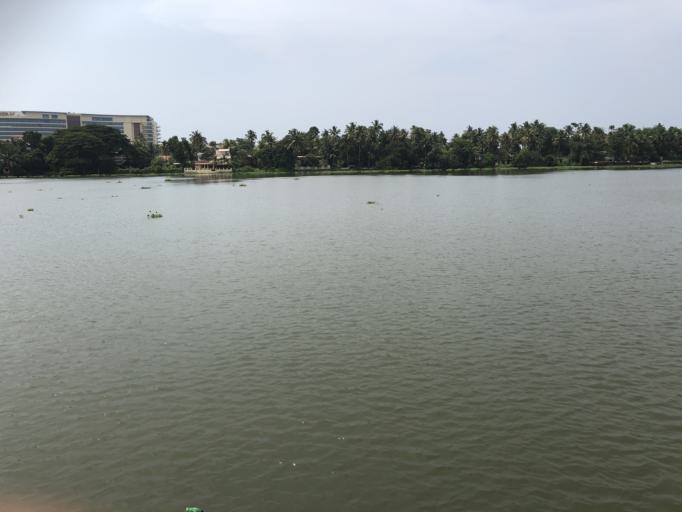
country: IN
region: Kerala
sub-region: Ernakulam
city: Cochin
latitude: 9.9892
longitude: 76.2691
